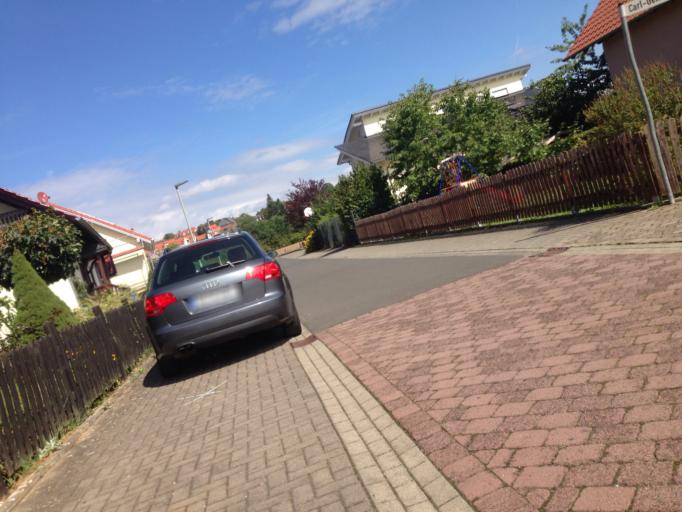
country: DE
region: Hesse
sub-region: Regierungsbezirk Giessen
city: Grunberg
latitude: 50.5847
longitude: 8.9568
